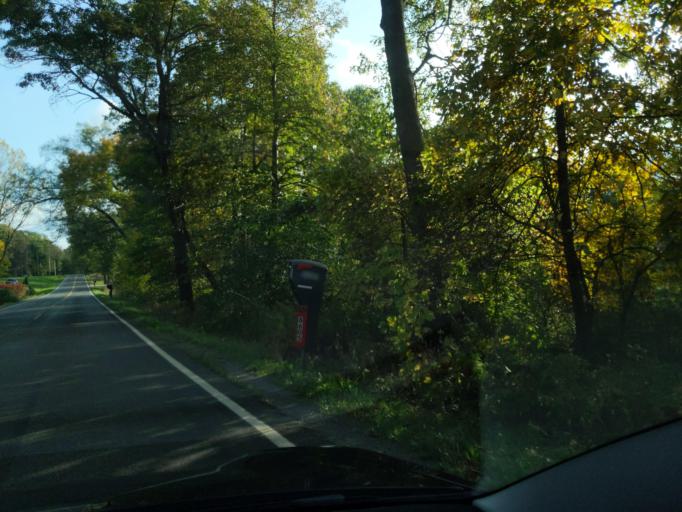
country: US
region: Michigan
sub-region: Ingham County
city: Leslie
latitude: 42.3633
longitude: -84.4629
